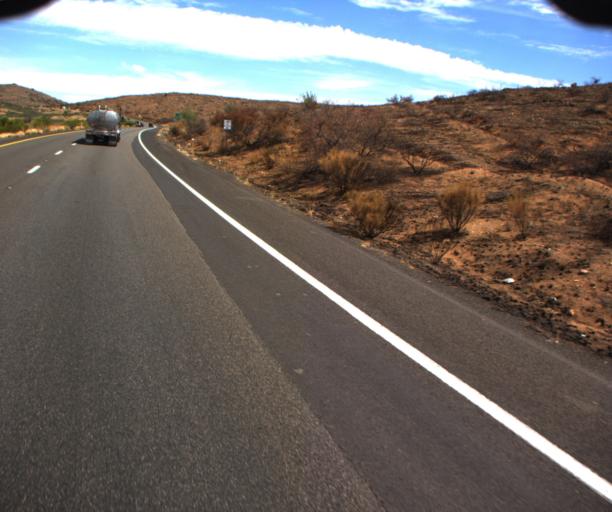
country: US
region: Arizona
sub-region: Yavapai County
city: Cordes Lakes
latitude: 34.2894
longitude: -112.1234
